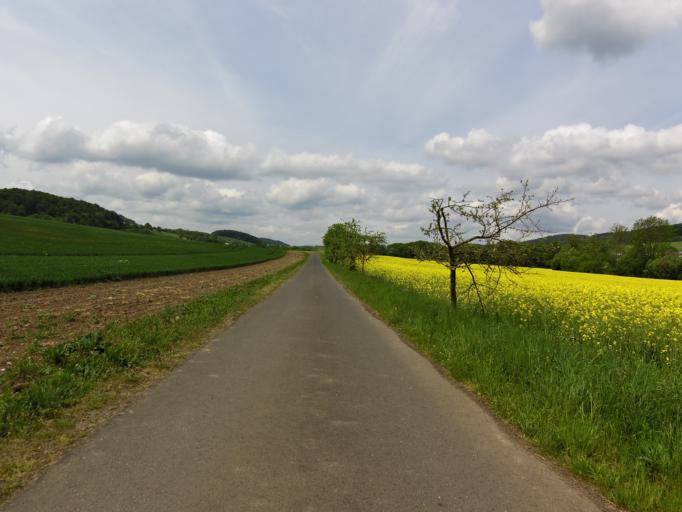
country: DE
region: Thuringia
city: Ifta
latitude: 51.0537
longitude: 10.1942
